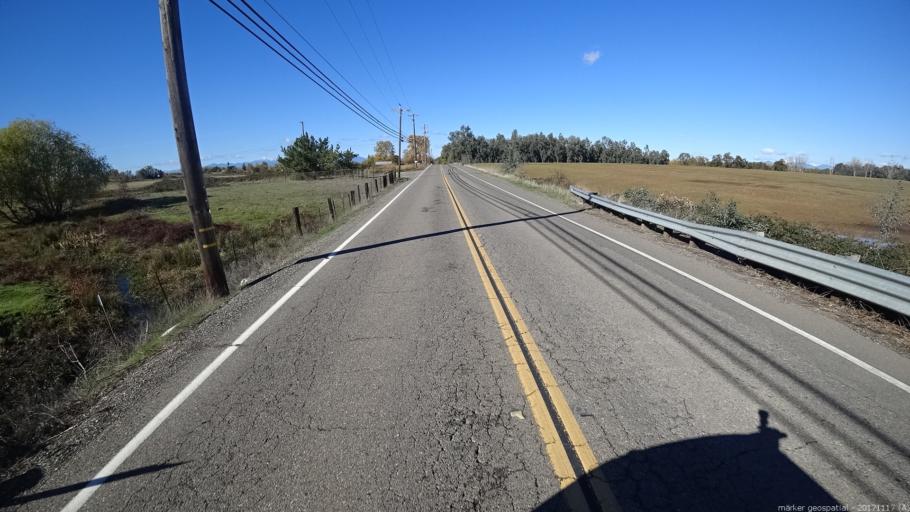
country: US
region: California
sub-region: Shasta County
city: Anderson
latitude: 40.4365
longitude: -122.2399
